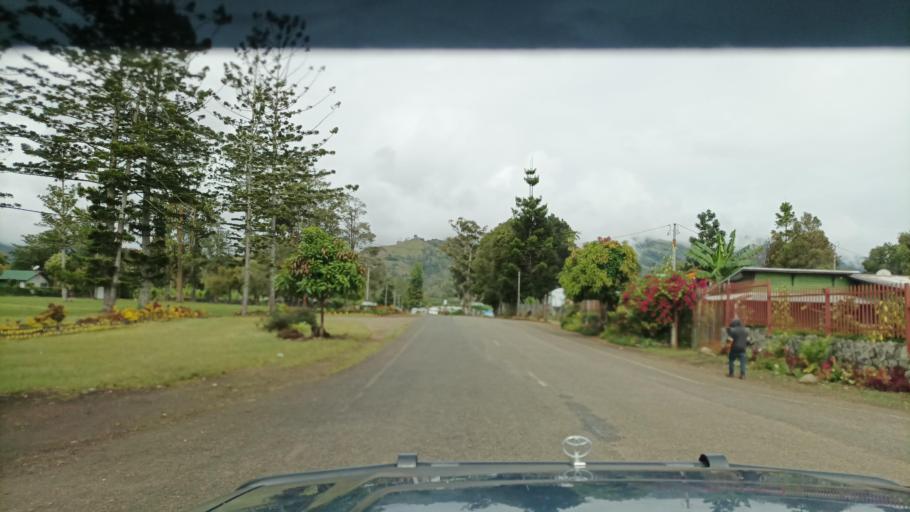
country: PG
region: Jiwaka
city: Minj
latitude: -5.9080
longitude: 144.6900
